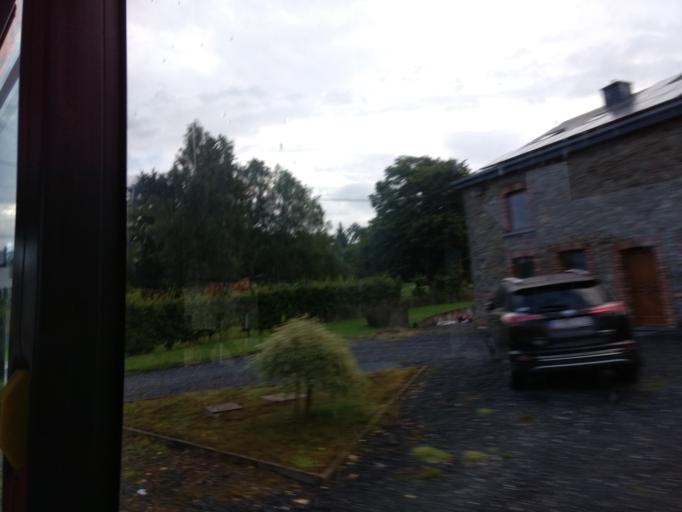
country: BE
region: Wallonia
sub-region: Province du Luxembourg
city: La Roche-en-Ardenne
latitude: 50.1768
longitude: 5.6663
